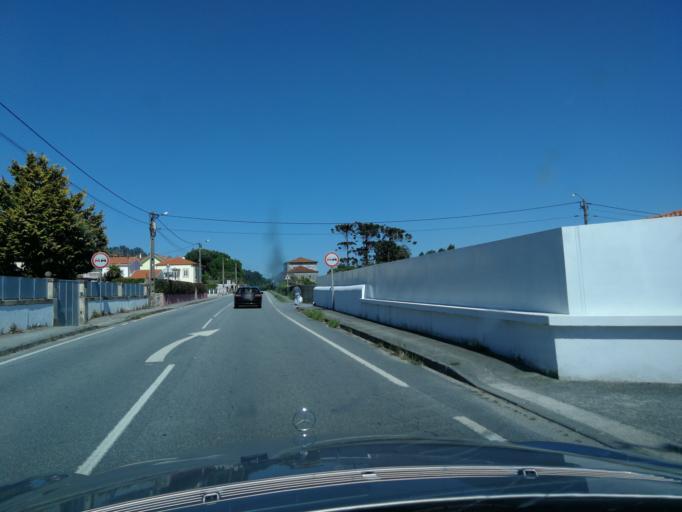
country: PT
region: Viana do Castelo
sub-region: Viana do Castelo
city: Darque
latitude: 41.7103
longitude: -8.7650
